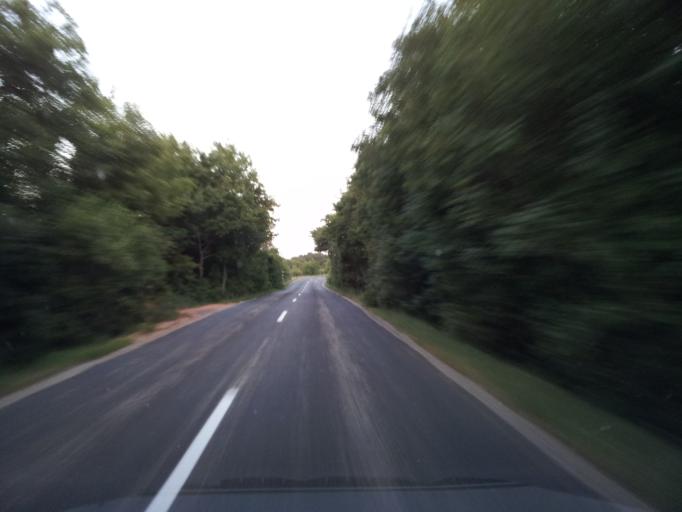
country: HU
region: Fejer
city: Szarliget
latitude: 47.5096
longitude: 18.5477
